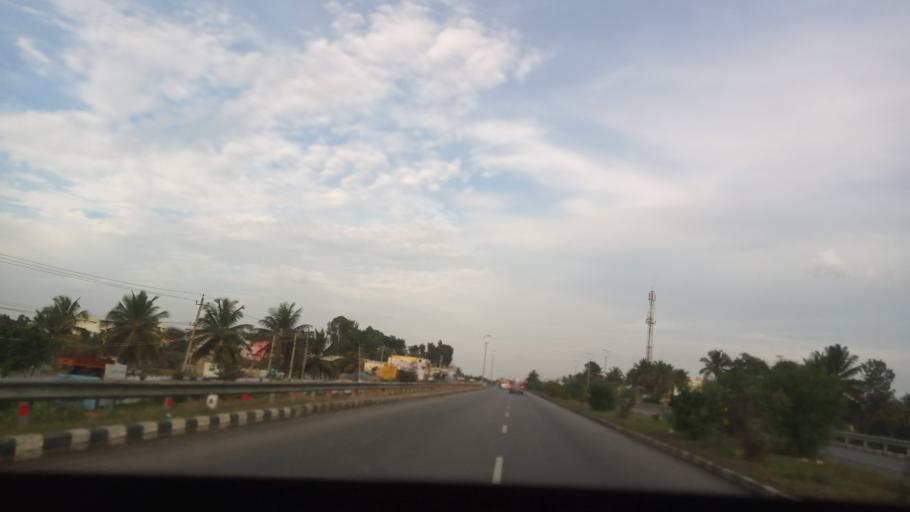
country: IN
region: Karnataka
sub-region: Bangalore Rural
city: Nelamangala
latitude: 13.0619
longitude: 77.3433
